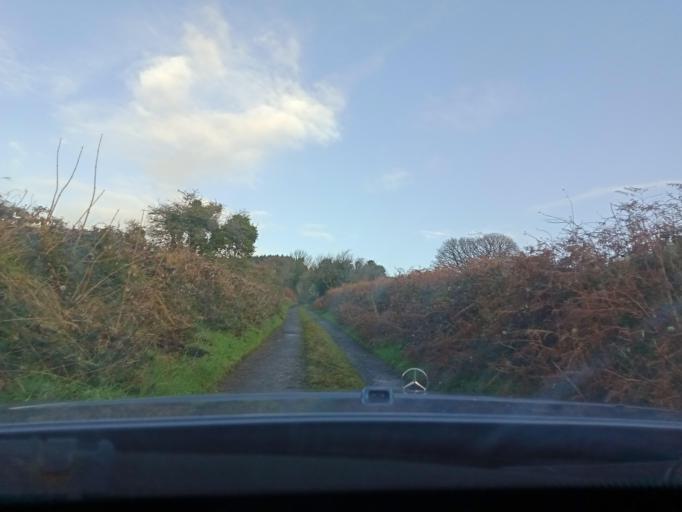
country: IE
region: Leinster
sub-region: Kilkenny
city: Callan
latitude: 52.4595
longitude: -7.4304
